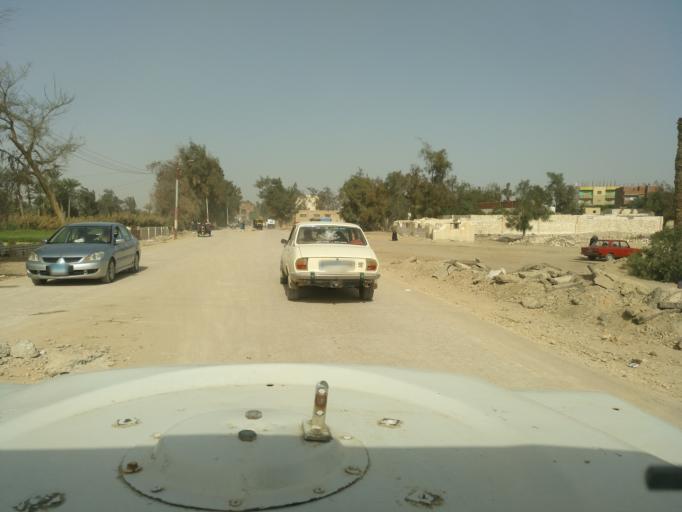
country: EG
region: Al Buhayrah
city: Beheira
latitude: 30.3687
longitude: 30.3584
